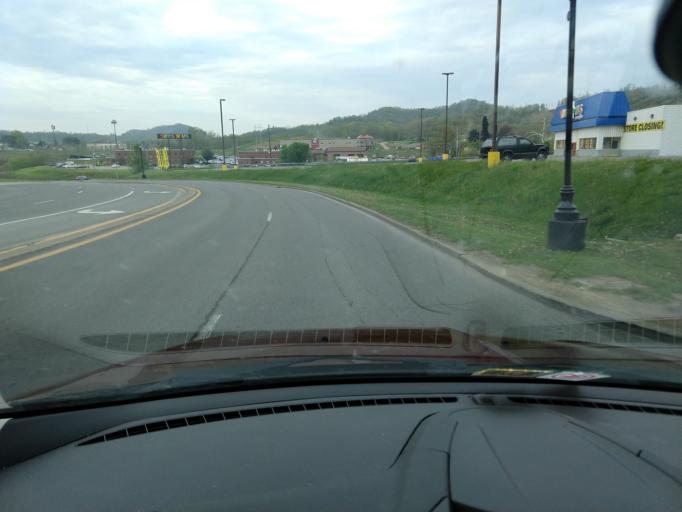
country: US
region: West Virginia
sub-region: Harrison County
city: Bridgeport
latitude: 39.3106
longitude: -80.2774
